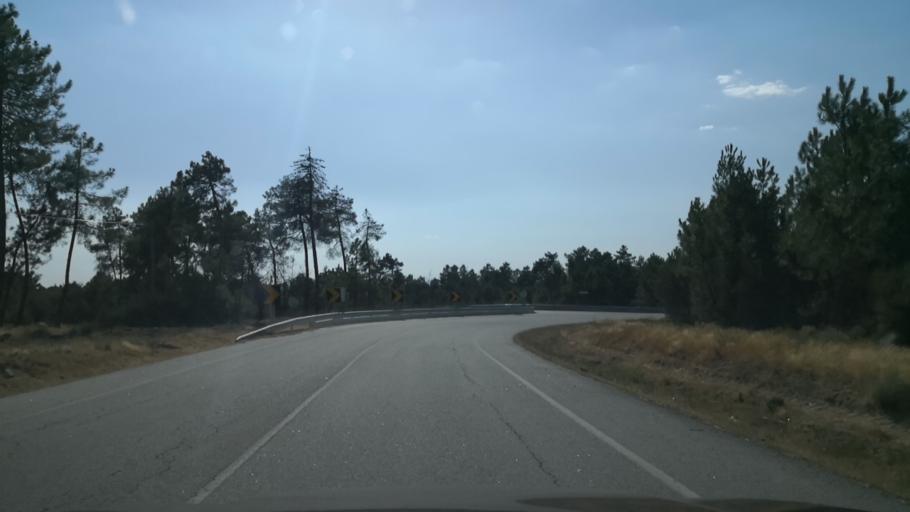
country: PT
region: Vila Real
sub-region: Murca
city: Murca
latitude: 41.3529
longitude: -7.4840
